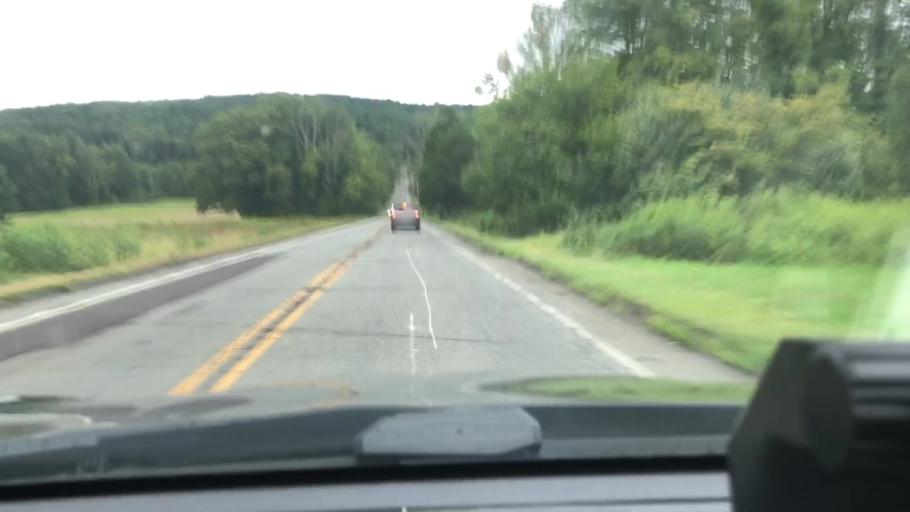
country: US
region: Pennsylvania
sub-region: Montgomery County
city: Gilbertsville
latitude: 40.3388
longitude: -75.5482
